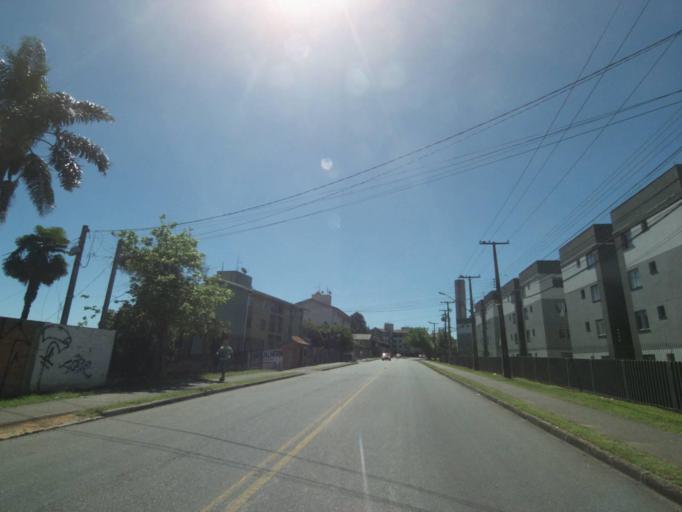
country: BR
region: Parana
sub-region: Curitiba
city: Curitiba
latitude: -25.4717
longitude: -49.3418
